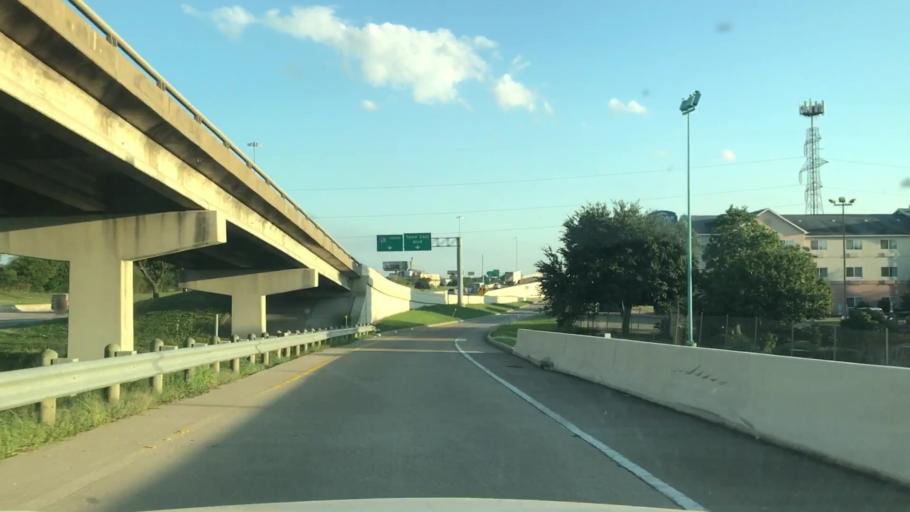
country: US
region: Texas
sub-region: Dallas County
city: Mesquite
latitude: 32.8205
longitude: -96.6299
